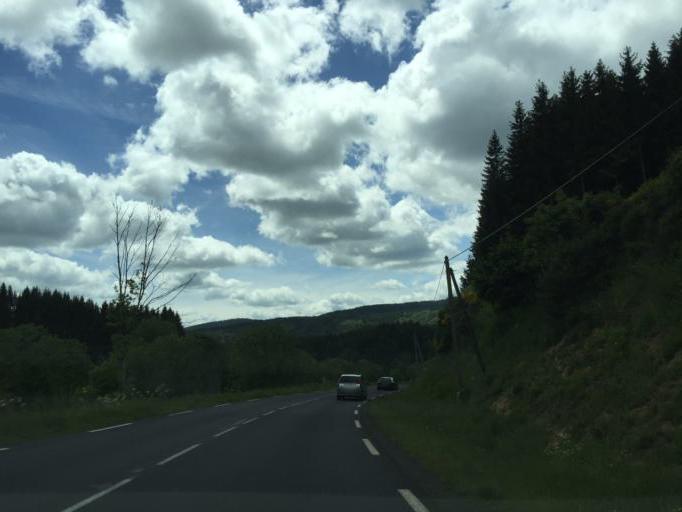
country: FR
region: Rhone-Alpes
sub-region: Departement de la Loire
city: Montbrison
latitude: 45.5363
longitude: 3.9280
